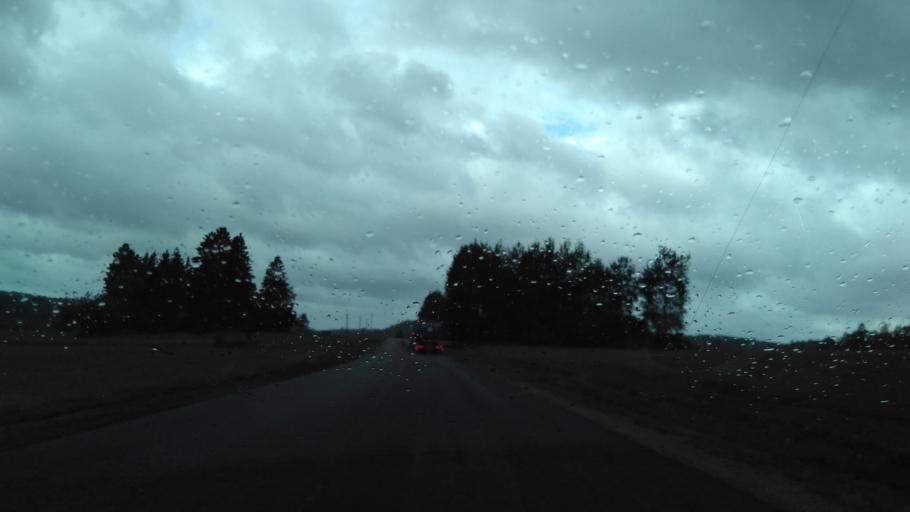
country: SE
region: Vaestra Goetaland
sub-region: Marks Kommun
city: Fritsla
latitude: 57.5710
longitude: 12.8338
